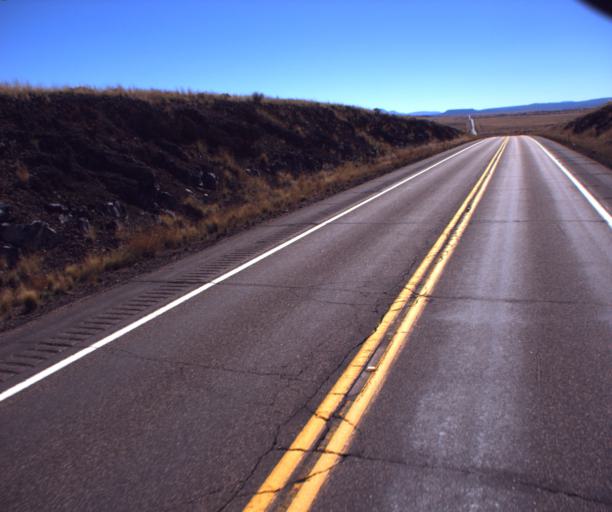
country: US
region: Arizona
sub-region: Apache County
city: Springerville
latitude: 34.2997
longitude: -109.3763
